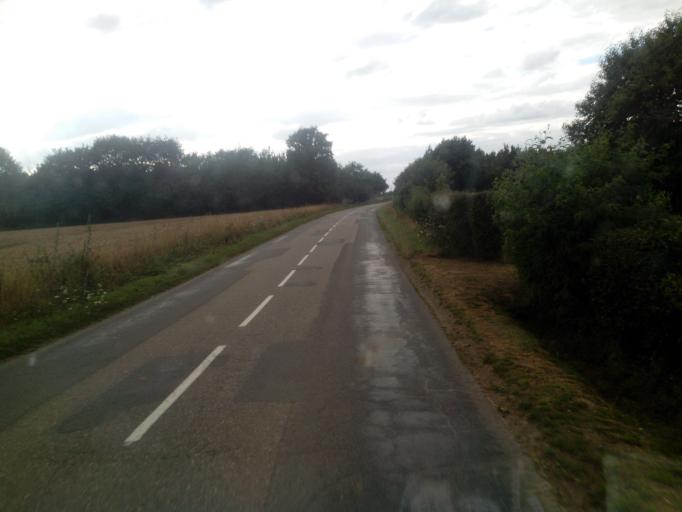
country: FR
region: Brittany
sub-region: Departement d'Ille-et-Vilaine
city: Plelan-le-Grand
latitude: 47.9928
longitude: -2.0709
